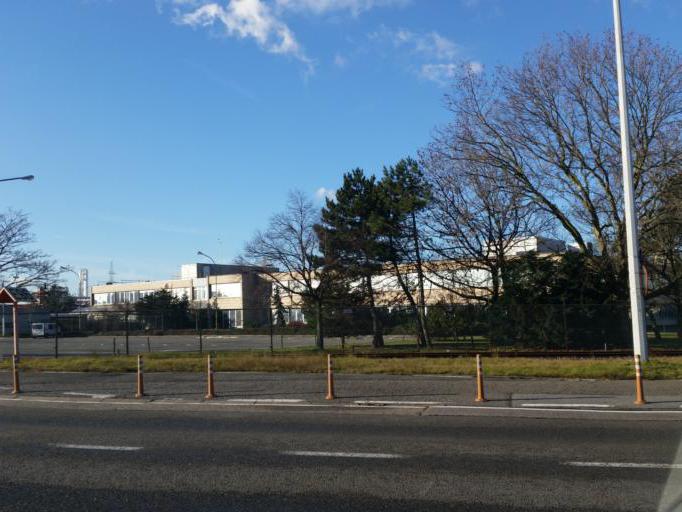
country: BE
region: Flanders
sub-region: Provincie Antwerpen
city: Zwijndrecht
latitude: 51.2414
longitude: 4.3381
